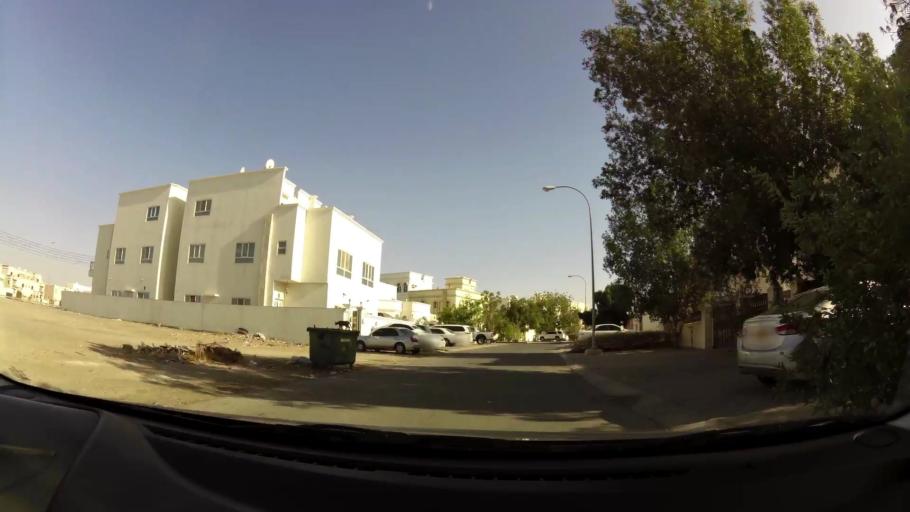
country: OM
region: Muhafazat Masqat
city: As Sib al Jadidah
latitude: 23.5997
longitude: 58.2163
